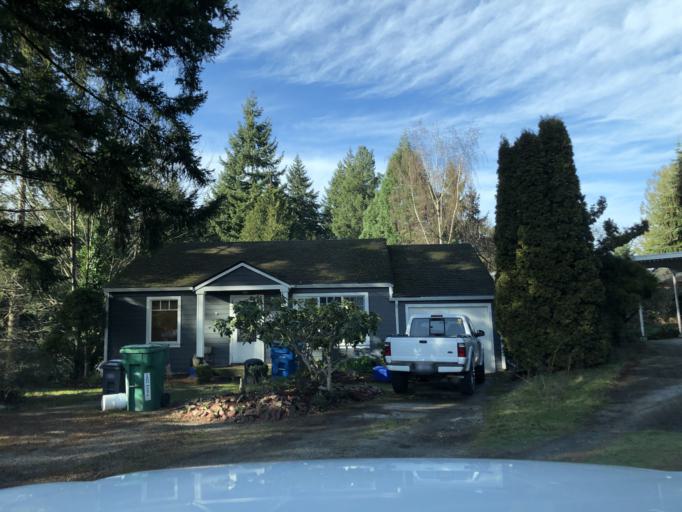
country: US
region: Washington
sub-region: King County
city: Lake Forest Park
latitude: 47.7199
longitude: -122.3029
